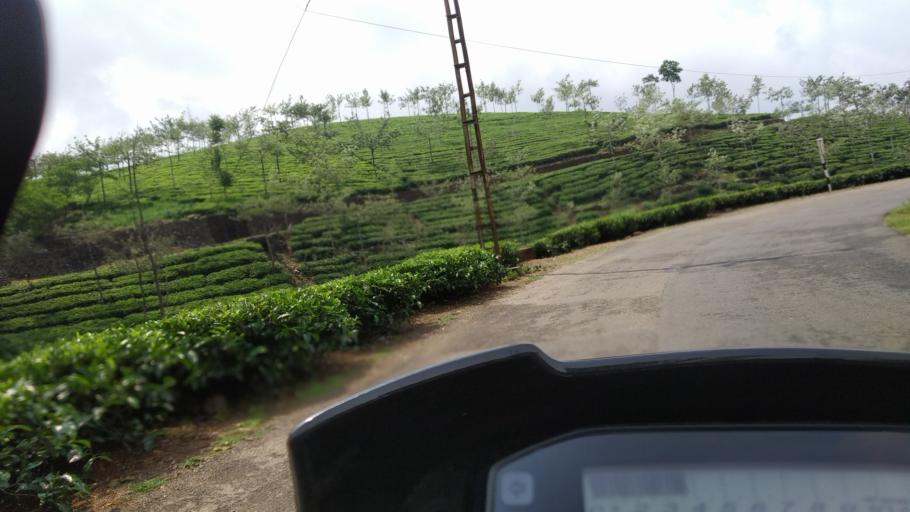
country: IN
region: Kerala
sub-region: Kottayam
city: Erattupetta
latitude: 9.6275
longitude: 76.9756
